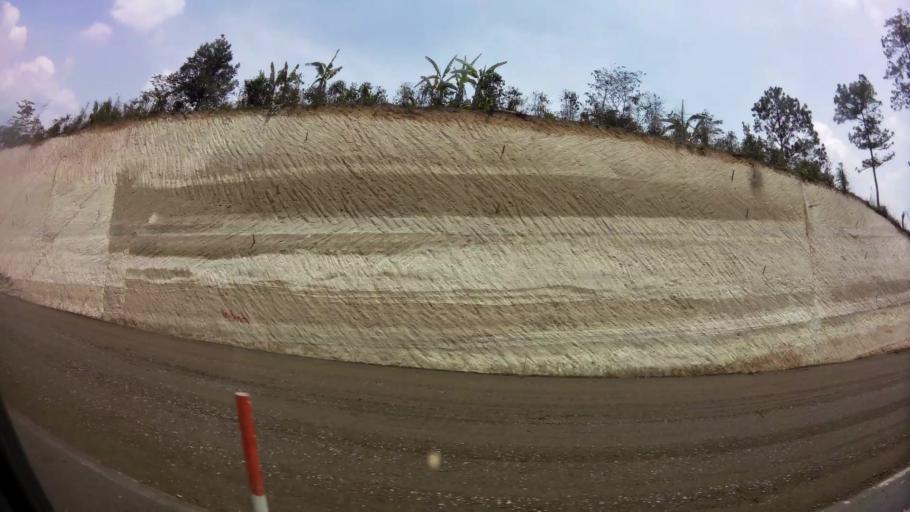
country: HN
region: Comayagua
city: El Socorro
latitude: 14.6236
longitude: -87.9076
